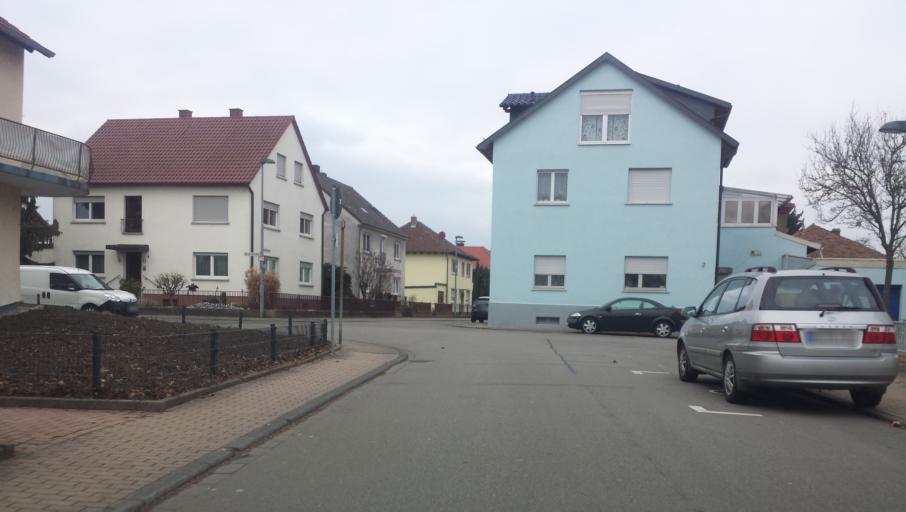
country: DE
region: Baden-Wuerttemberg
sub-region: Karlsruhe Region
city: Heddesheim
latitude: 49.5033
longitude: 8.5983
